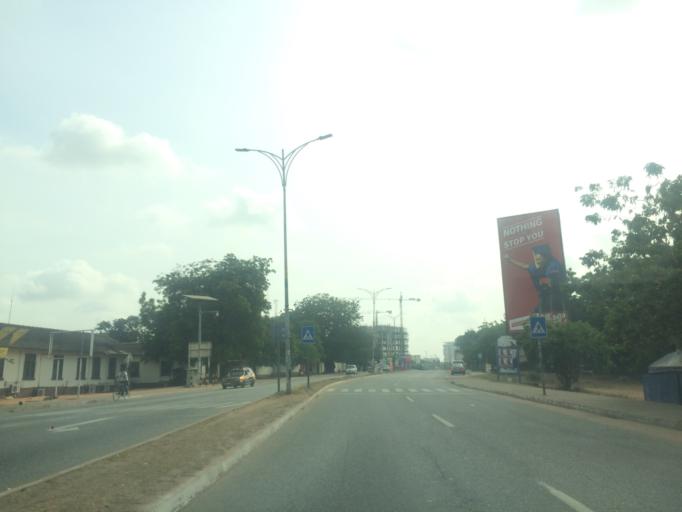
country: GH
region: Greater Accra
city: Accra
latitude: 5.5622
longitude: -0.2055
